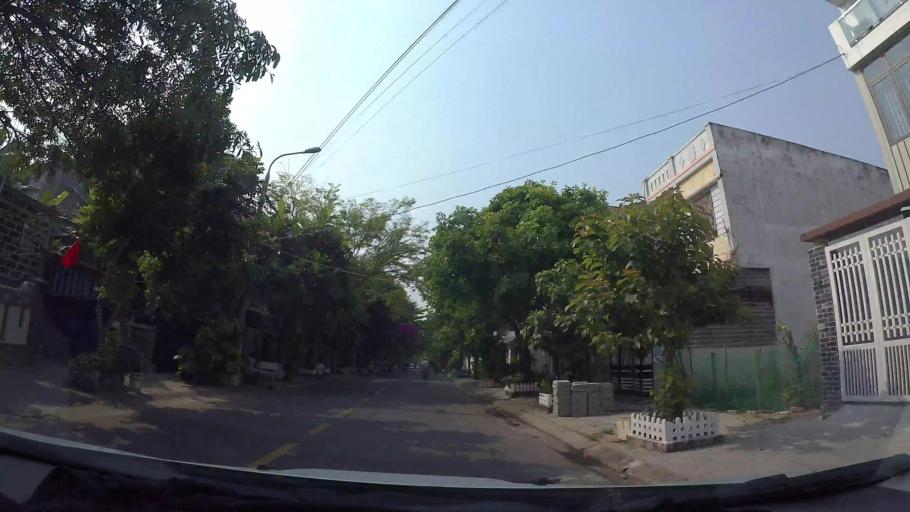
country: VN
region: Da Nang
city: Cam Le
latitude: 16.0013
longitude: 108.2149
